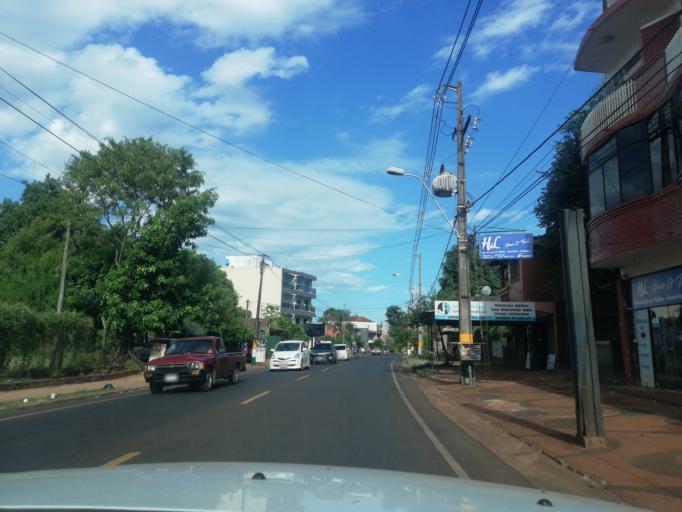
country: PY
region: Itapua
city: Encarnacion
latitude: -27.3429
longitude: -55.8488
